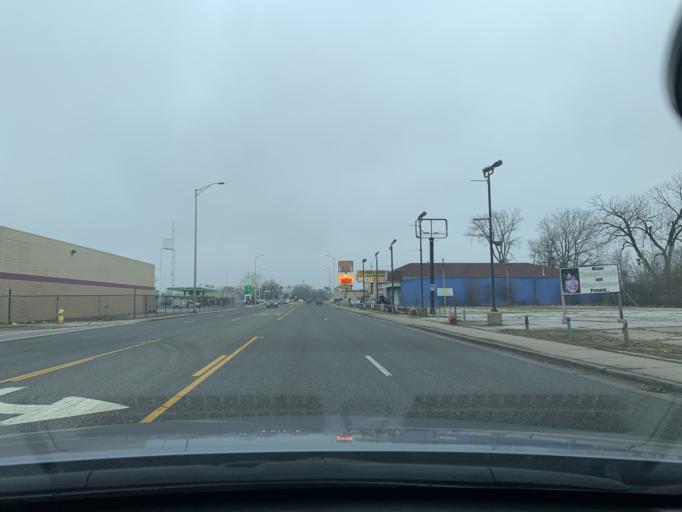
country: US
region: Illinois
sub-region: Cook County
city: Posen
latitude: 41.6226
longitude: -87.6716
